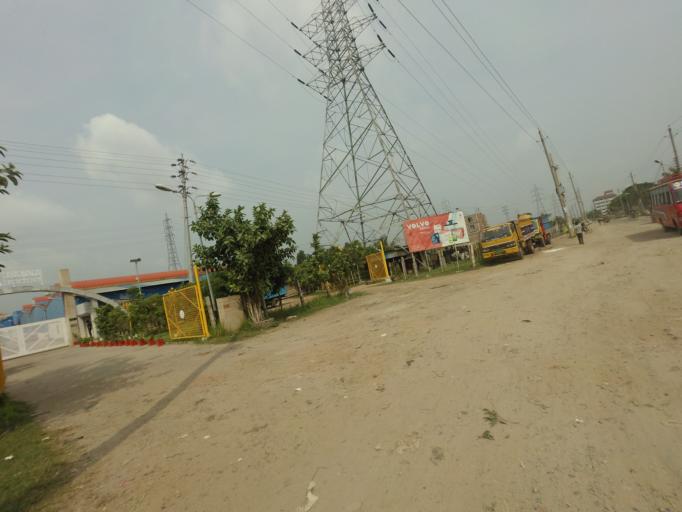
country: BD
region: Dhaka
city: Azimpur
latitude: 23.7250
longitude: 90.3697
